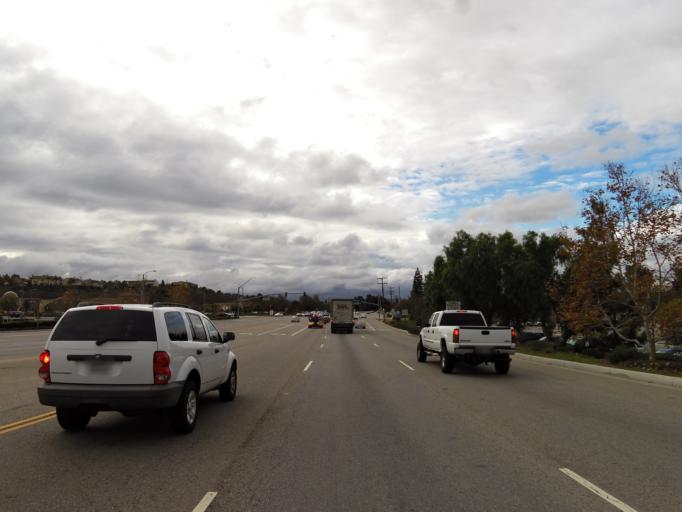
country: US
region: California
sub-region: Ventura County
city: Moorpark
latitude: 34.2802
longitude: -118.8677
